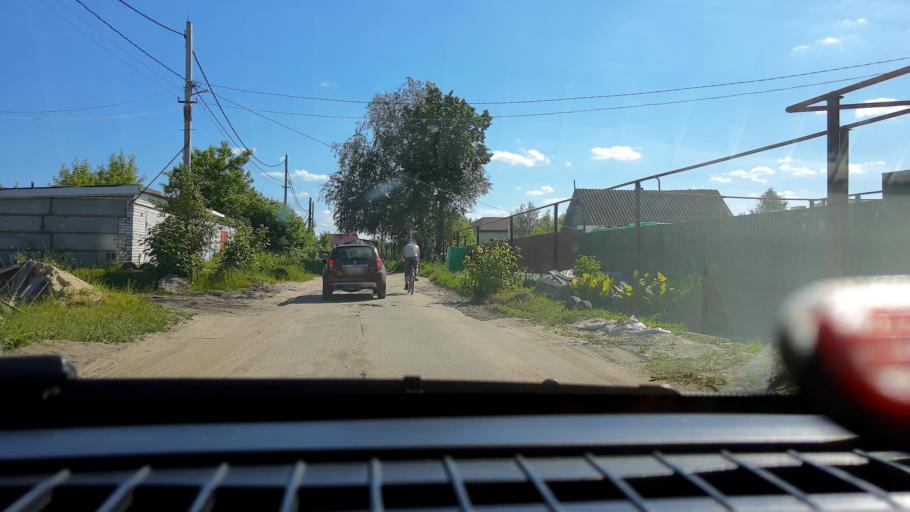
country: RU
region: Nizjnij Novgorod
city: Gidrotorf
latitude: 56.5130
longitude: 43.5363
